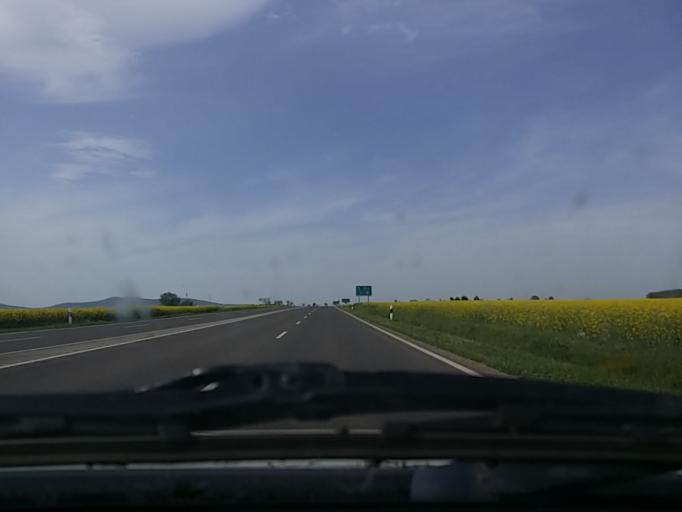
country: HU
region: Baranya
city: Kozarmisleny
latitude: 46.0044
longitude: 18.2351
